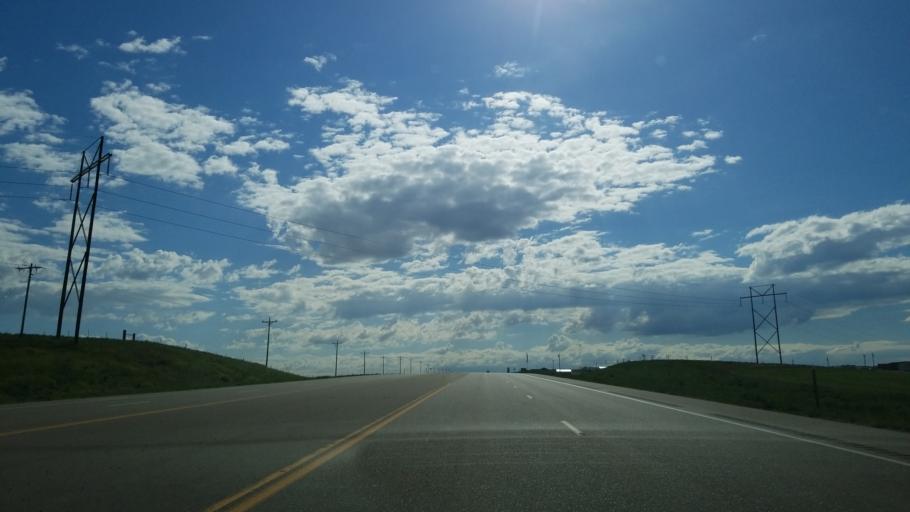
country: US
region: North Dakota
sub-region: McKenzie County
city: Watford City
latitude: 47.8049
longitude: -103.6098
